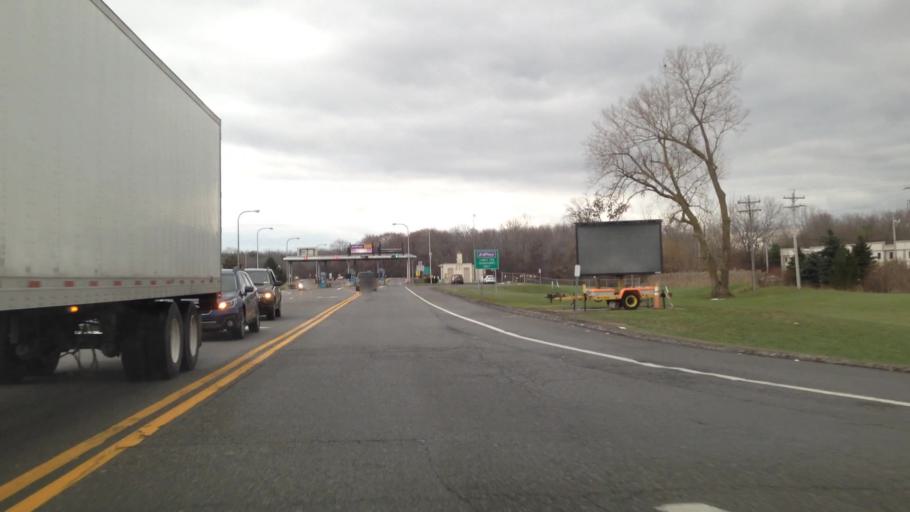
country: US
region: New York
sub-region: Genesee County
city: Batavia
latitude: 43.0160
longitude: -78.1918
